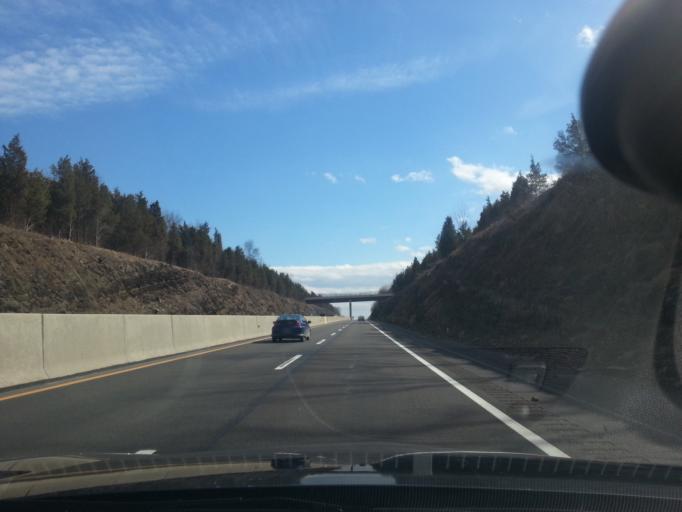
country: US
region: Pennsylvania
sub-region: Montgomery County
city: Woxall
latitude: 40.3526
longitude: -75.3920
